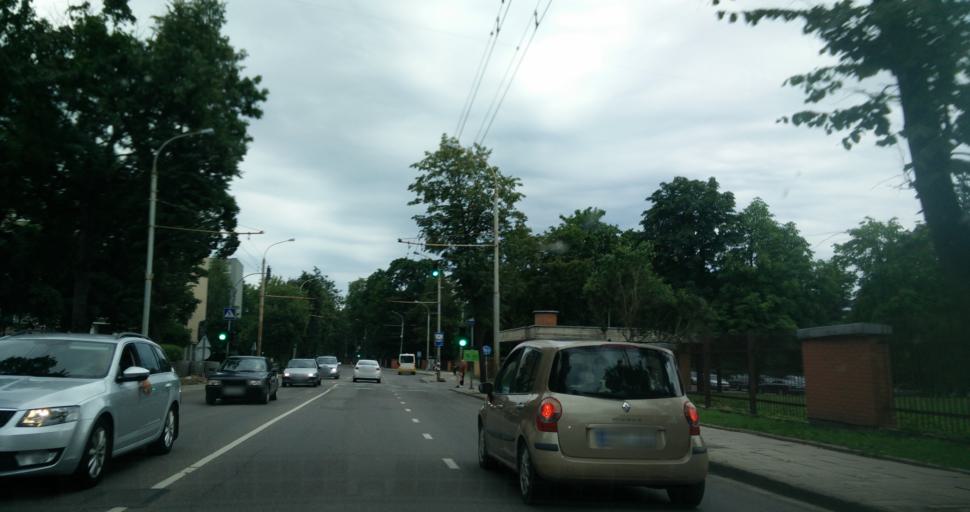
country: LT
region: Vilnius County
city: Rasos
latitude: 54.7207
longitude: 25.3179
